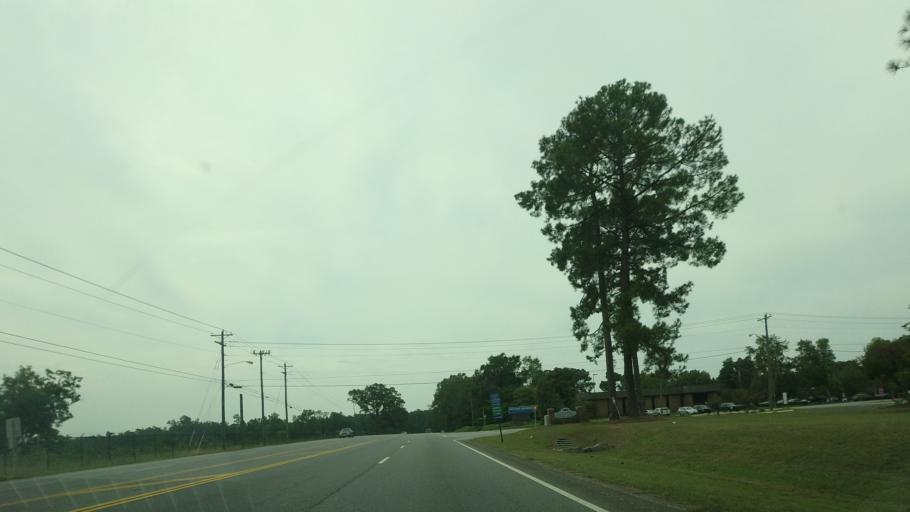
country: US
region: Georgia
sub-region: Houston County
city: Robins Air Force Base
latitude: 32.5829
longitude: -83.5874
